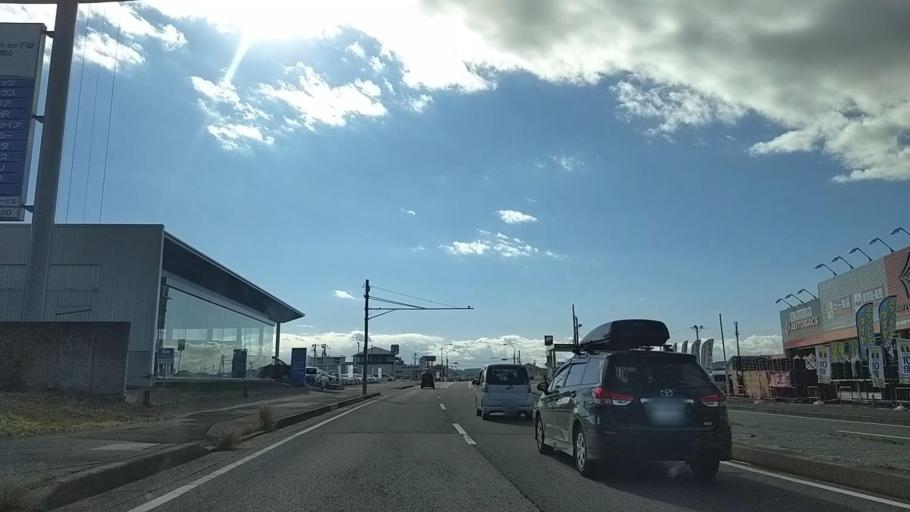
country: JP
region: Chiba
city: Tateyama
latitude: 35.0175
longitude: 139.8717
